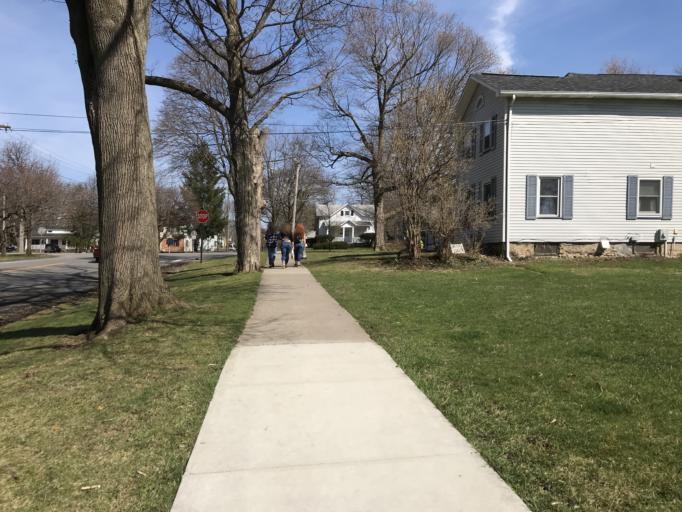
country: US
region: New York
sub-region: Livingston County
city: Geneseo
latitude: 42.7990
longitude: -77.8073
